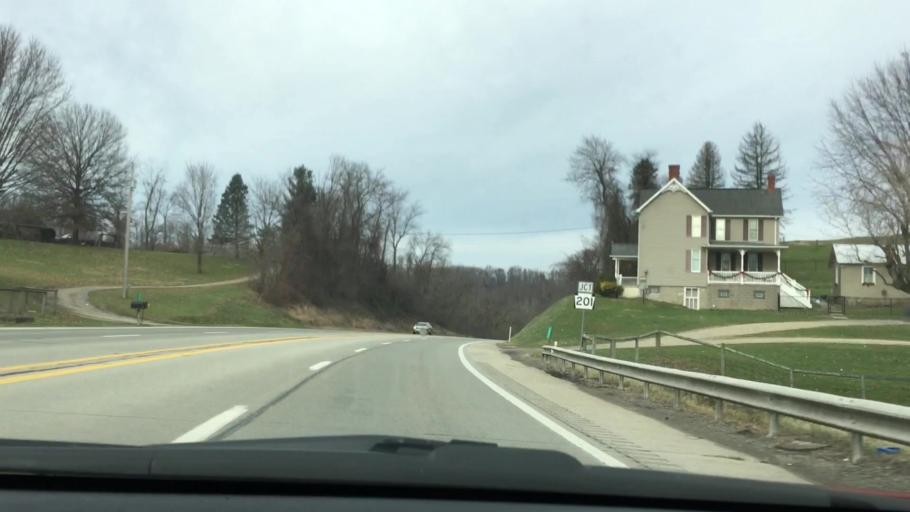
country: US
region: Pennsylvania
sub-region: Fayette County
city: Perryopolis
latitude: 40.0447
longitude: -79.7734
